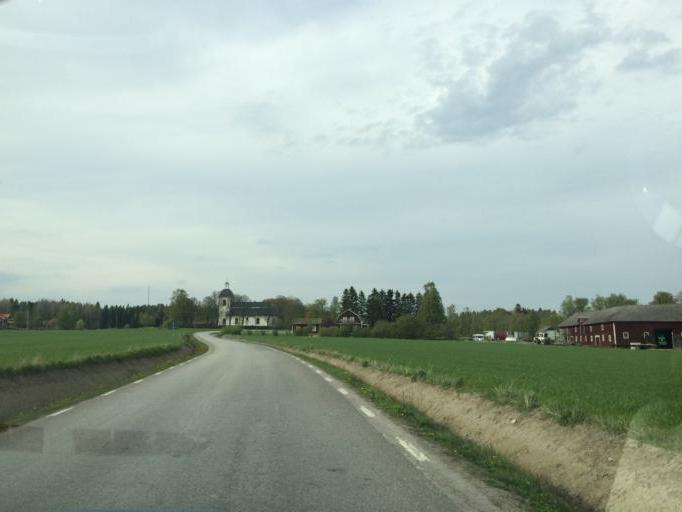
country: SE
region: Vaestmanland
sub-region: Kopings Kommun
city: Koping
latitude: 59.5802
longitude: 15.9871
